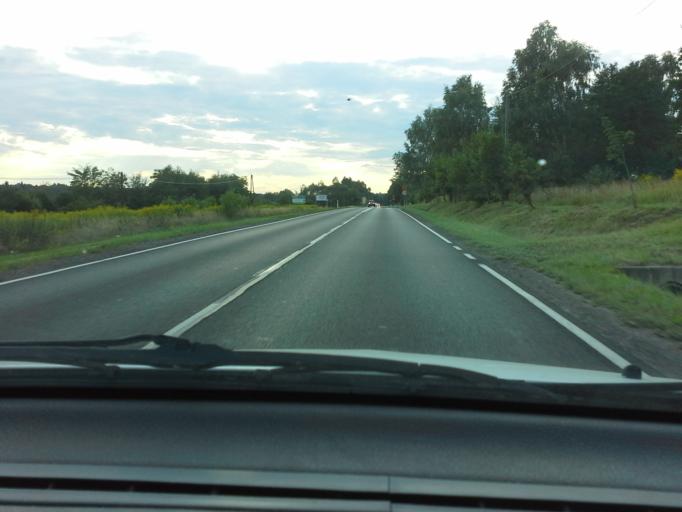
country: PL
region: Lesser Poland Voivodeship
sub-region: Powiat krakowski
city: Wola Filipowska
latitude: 50.1362
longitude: 19.5685
